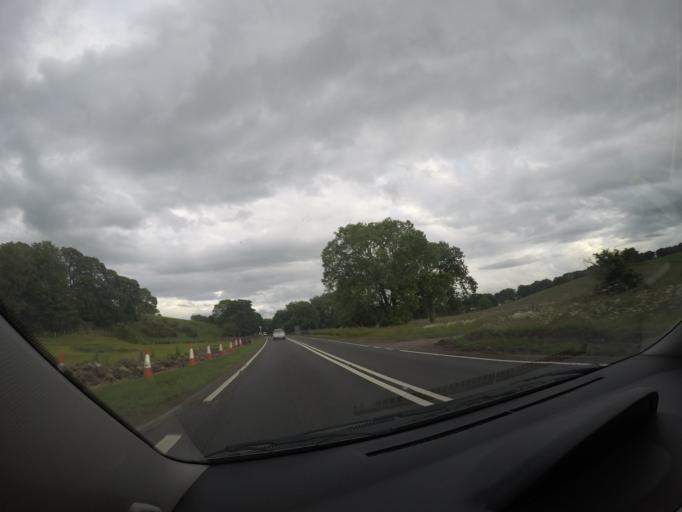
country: GB
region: England
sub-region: Cumbria
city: Kirkby Stephen
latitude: 54.5419
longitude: -2.3894
